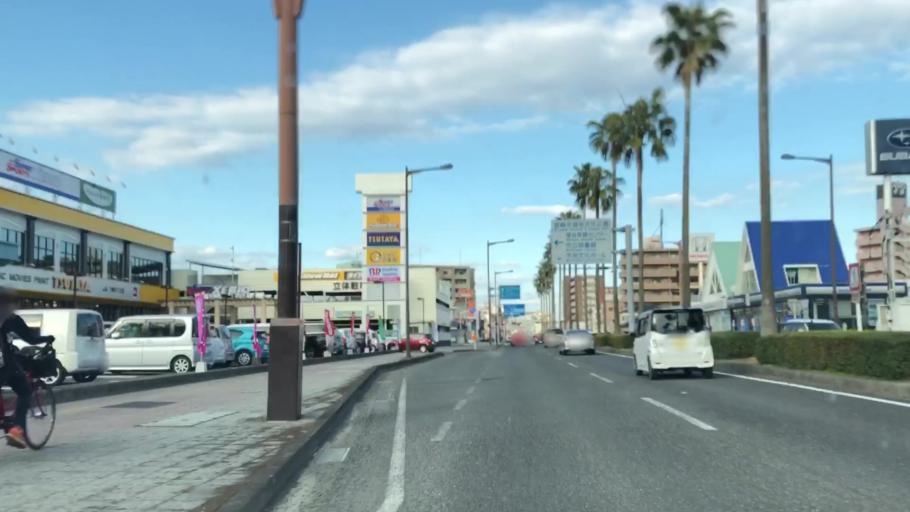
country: JP
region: Miyazaki
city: Miyazaki-shi
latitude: 31.8958
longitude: 131.4171
